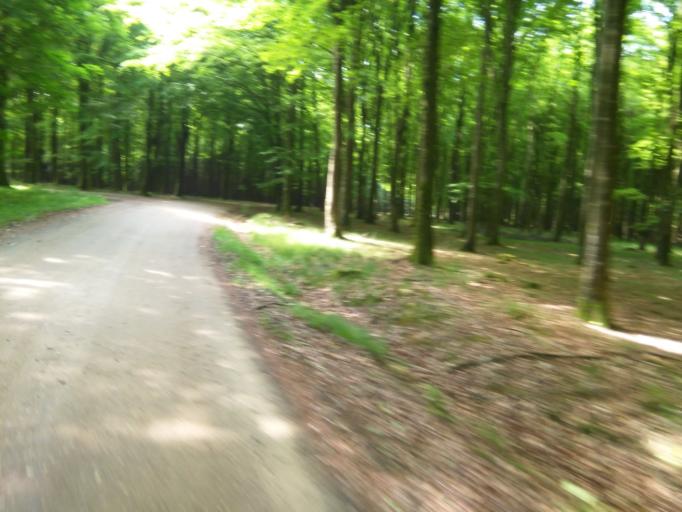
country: DK
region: Central Jutland
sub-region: Favrskov Kommune
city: Hammel
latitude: 56.2668
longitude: 9.9371
